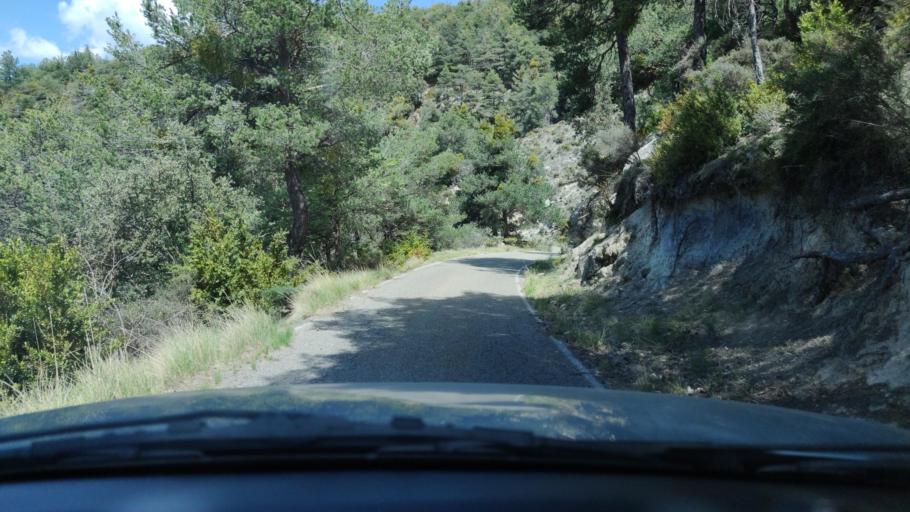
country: ES
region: Catalonia
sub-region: Provincia de Lleida
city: Sort
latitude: 42.3160
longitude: 1.1061
